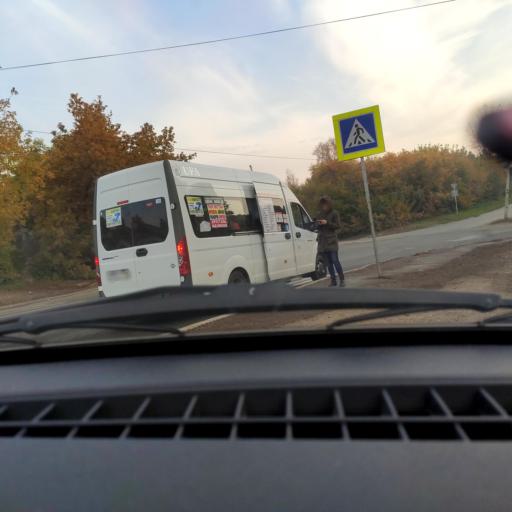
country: RU
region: Bashkortostan
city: Ufa
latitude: 54.7524
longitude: 55.9637
